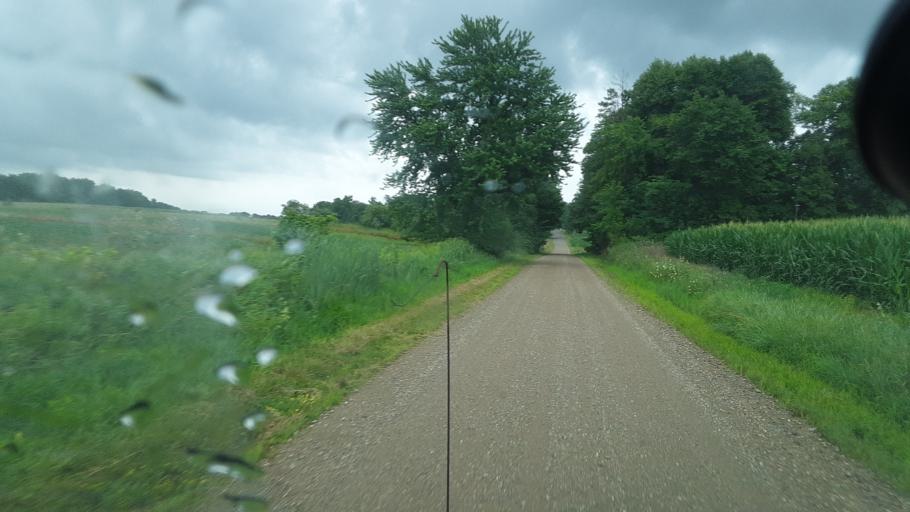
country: US
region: Indiana
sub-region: Steuben County
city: Hamilton
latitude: 41.5379
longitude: -84.8343
